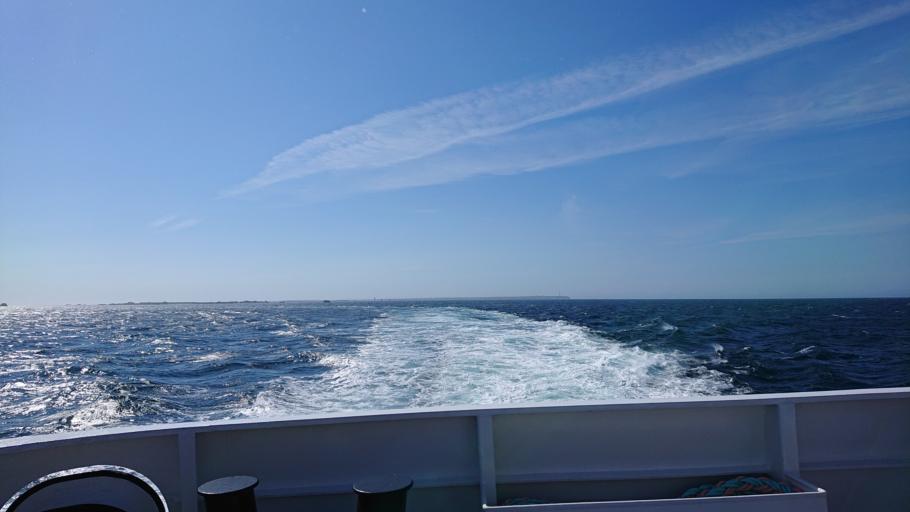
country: FR
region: Brittany
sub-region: Departement du Finistere
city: Le Conquet
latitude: 48.4141
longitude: -4.9388
